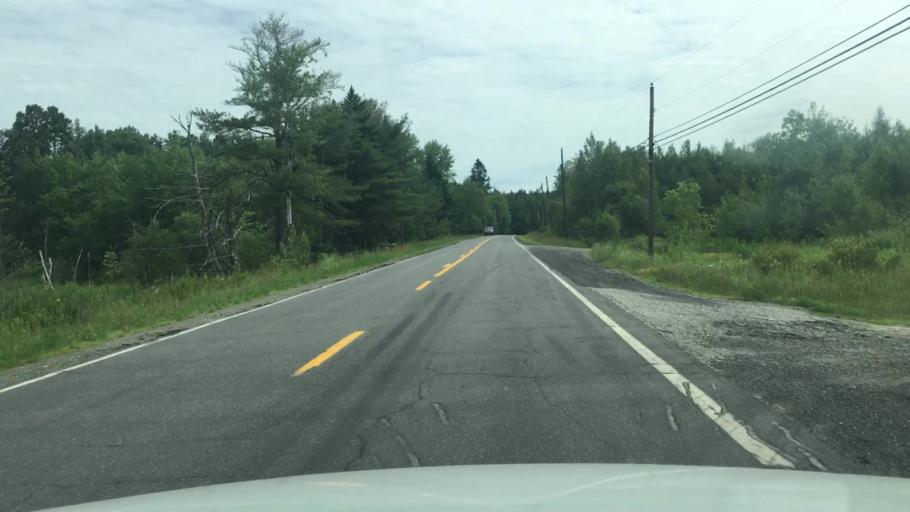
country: US
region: Maine
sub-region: Kennebec County
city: Clinton
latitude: 44.6044
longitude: -69.4592
